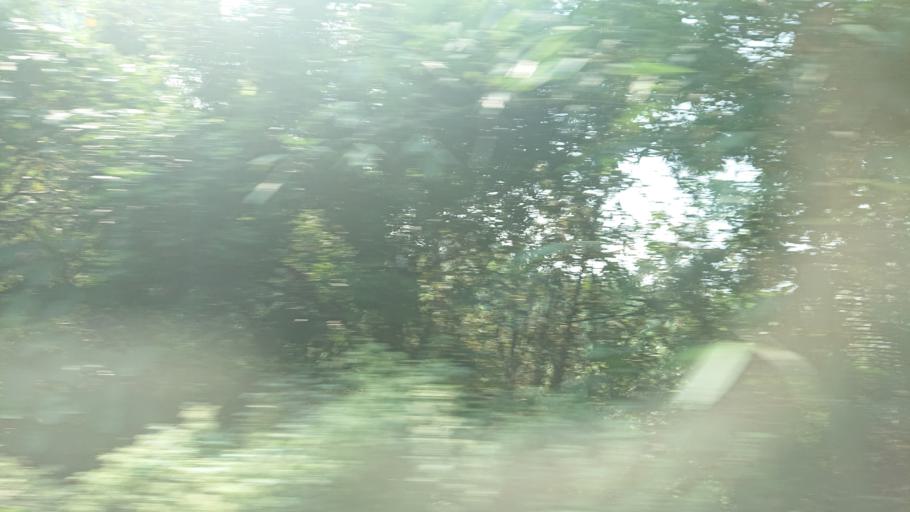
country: TW
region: Taiwan
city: Lugu
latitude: 23.7134
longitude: 120.6683
